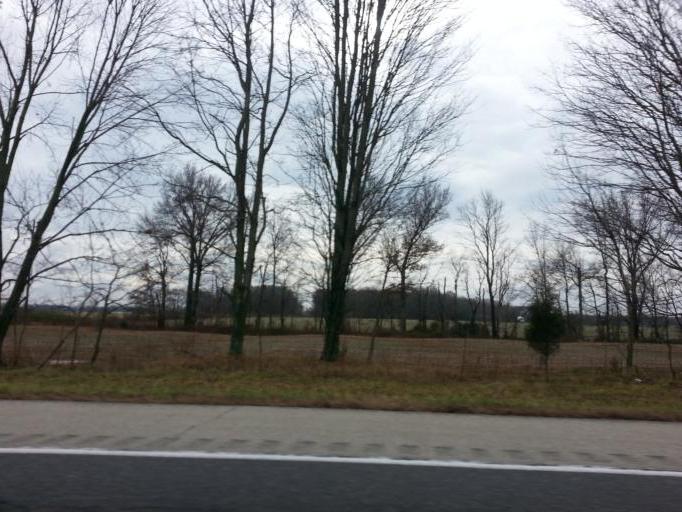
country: US
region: Indiana
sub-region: Ripley County
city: Batesville
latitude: 39.3166
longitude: -85.2831
